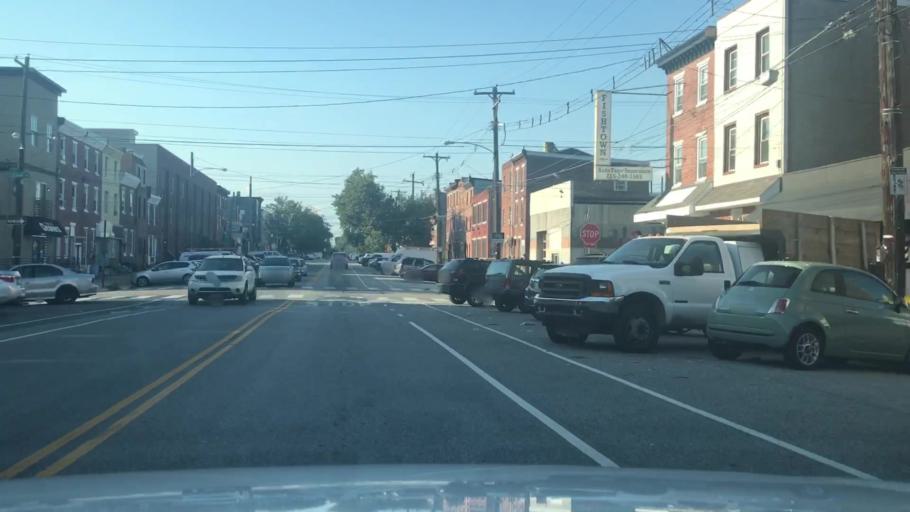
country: US
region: Pennsylvania
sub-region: Philadelphia County
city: Philadelphia
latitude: 39.9779
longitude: -75.1245
